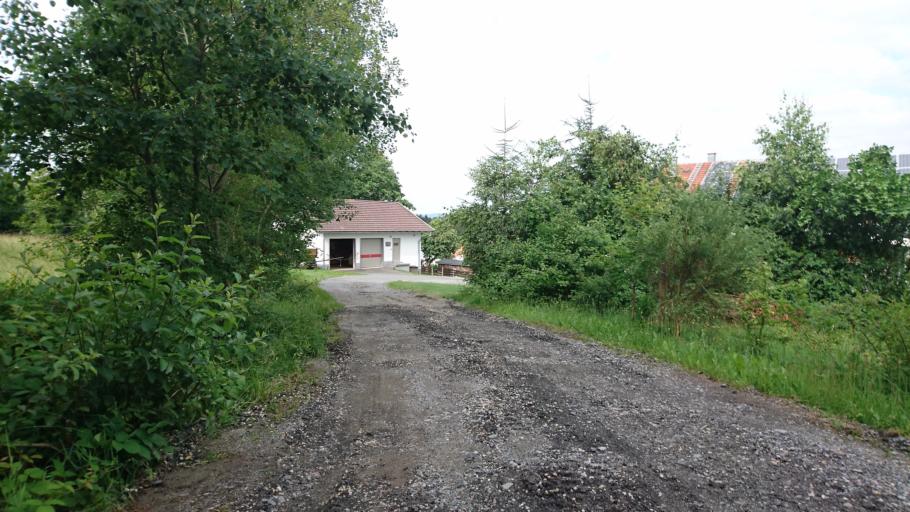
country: DE
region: Bavaria
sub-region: Lower Bavaria
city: Neuschonau
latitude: 48.8781
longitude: 13.4761
